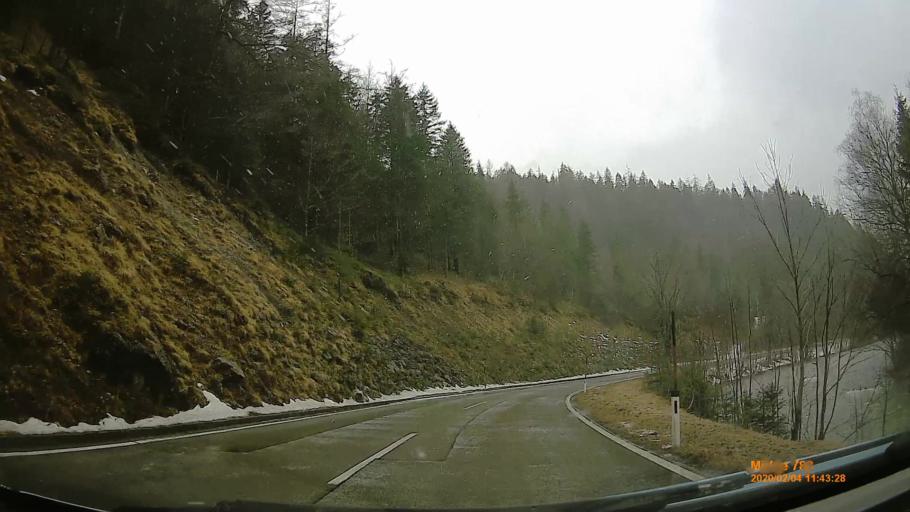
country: AT
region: Styria
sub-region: Politischer Bezirk Bruck-Muerzzuschlag
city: Muerzsteg
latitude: 47.6805
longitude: 15.4854
